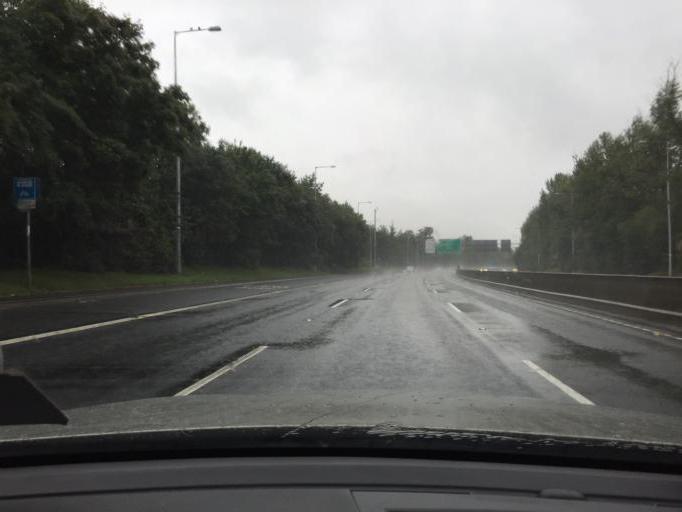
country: IE
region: Leinster
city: Lucan
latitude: 53.3530
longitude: -6.4340
